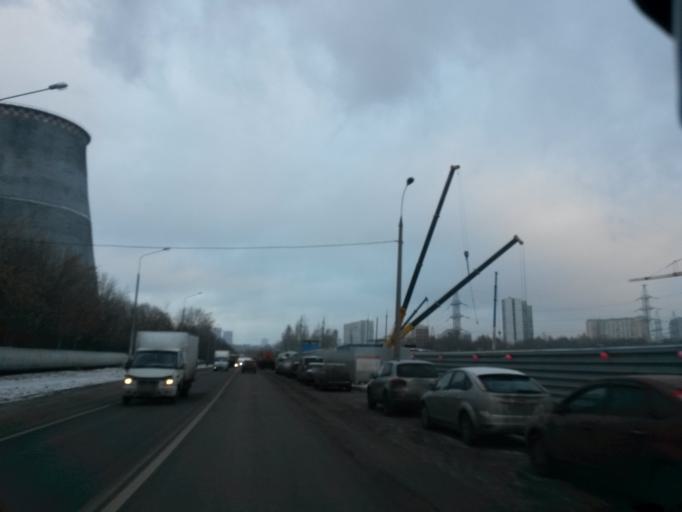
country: RU
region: Moscow
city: Amin'yevo
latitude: 55.6982
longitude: 37.4521
